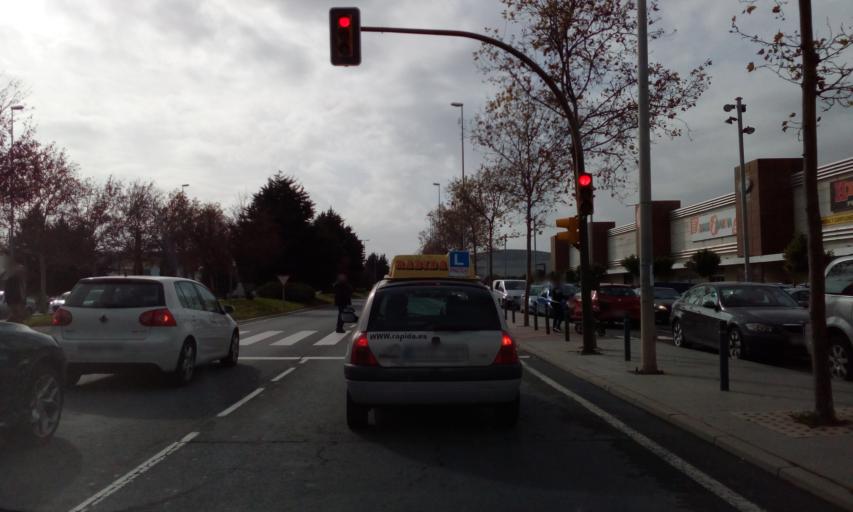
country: ES
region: Andalusia
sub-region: Provincia de Huelva
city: Huelva
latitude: 37.2652
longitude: -6.9583
